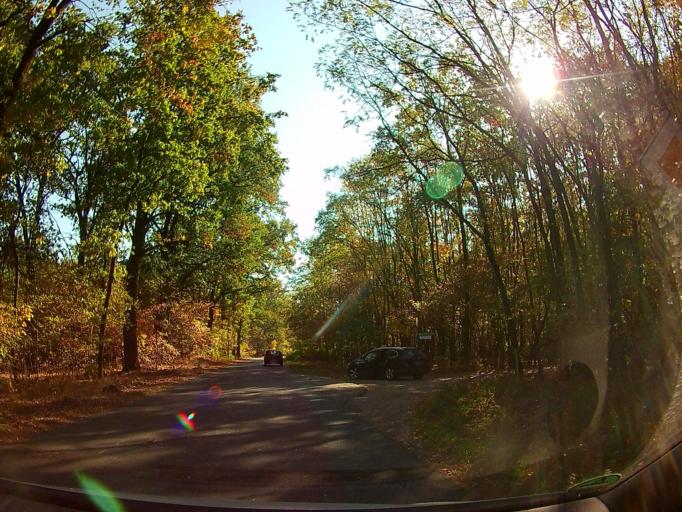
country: DE
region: Brandenburg
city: Zossen
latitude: 52.1425
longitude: 13.4924
